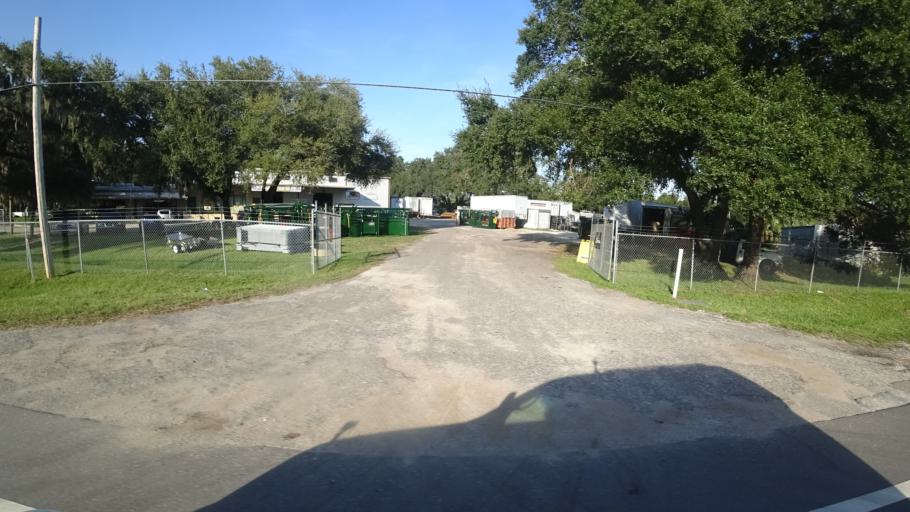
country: US
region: Florida
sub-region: Manatee County
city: West Samoset
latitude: 27.4628
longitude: -82.5585
